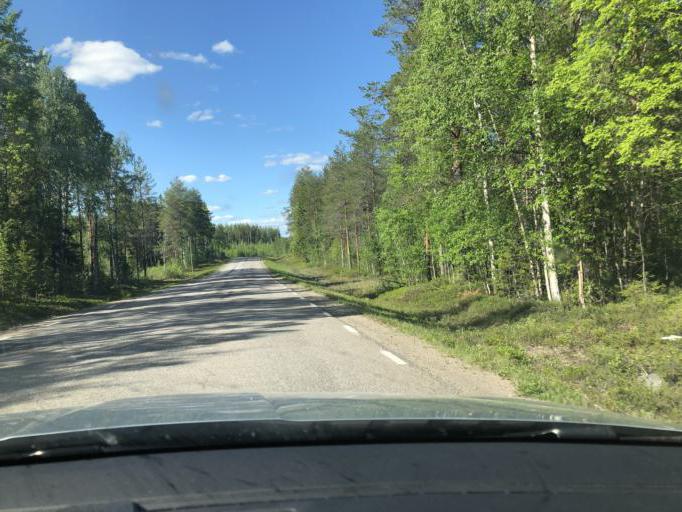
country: SE
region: Norrbotten
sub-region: Kalix Kommun
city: Kalix
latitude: 65.8845
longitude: 23.1520
